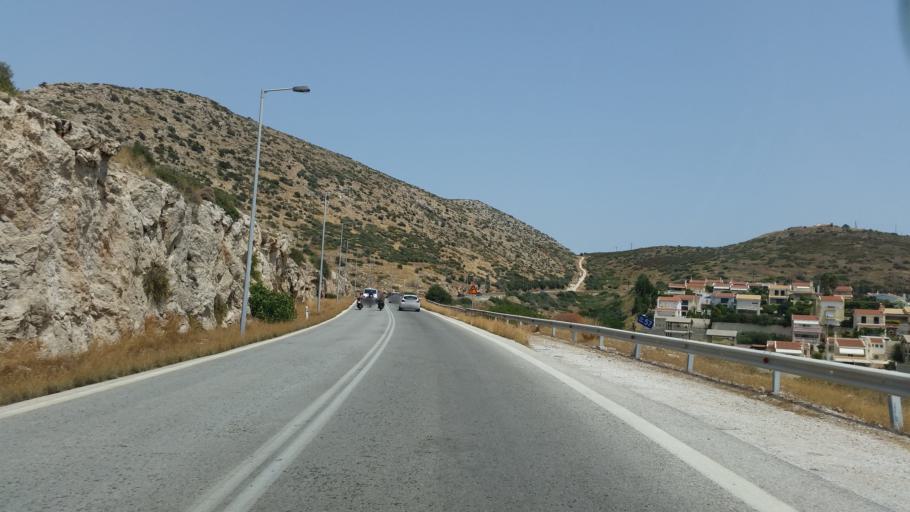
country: GR
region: Attica
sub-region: Nomarchia Anatolikis Attikis
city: Palaia Fokaia
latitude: 37.6826
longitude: 23.9415
